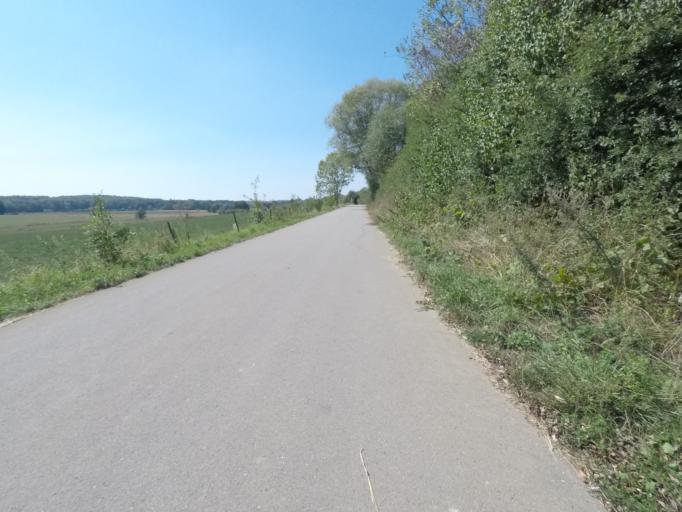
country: LU
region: Luxembourg
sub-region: Canton de Capellen
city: Steinfort
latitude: 49.6333
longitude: 5.9074
